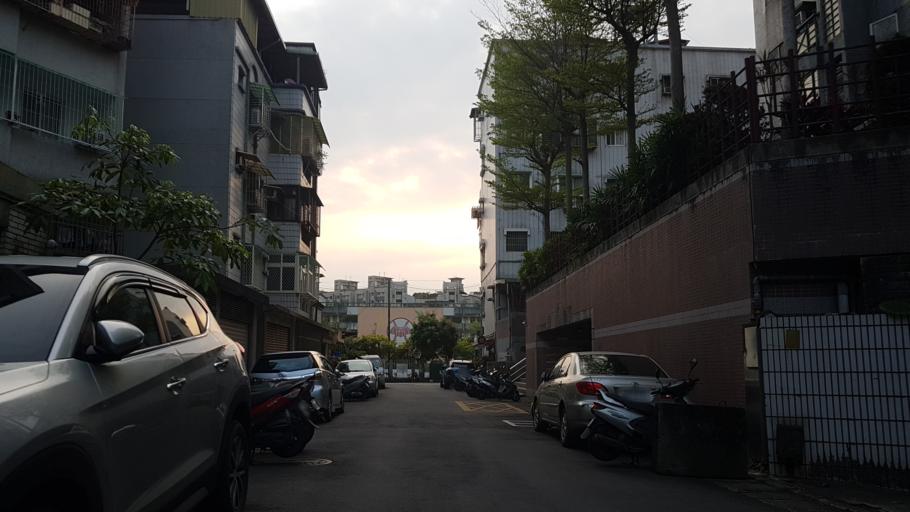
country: TW
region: Taipei
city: Taipei
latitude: 25.0052
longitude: 121.5515
